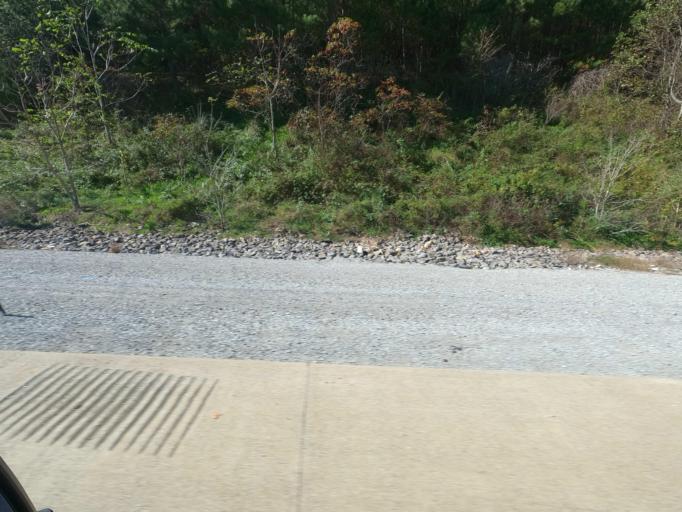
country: US
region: Tennessee
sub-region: Williamson County
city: Fairview
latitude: 35.9372
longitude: -87.1900
